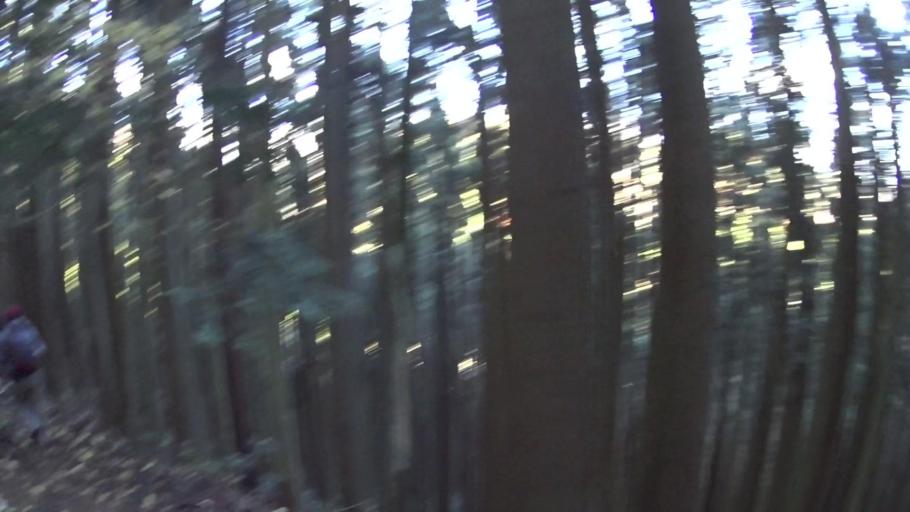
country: JP
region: Kyoto
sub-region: Kyoto-shi
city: Kamigyo-ku
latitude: 35.0862
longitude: 135.7396
